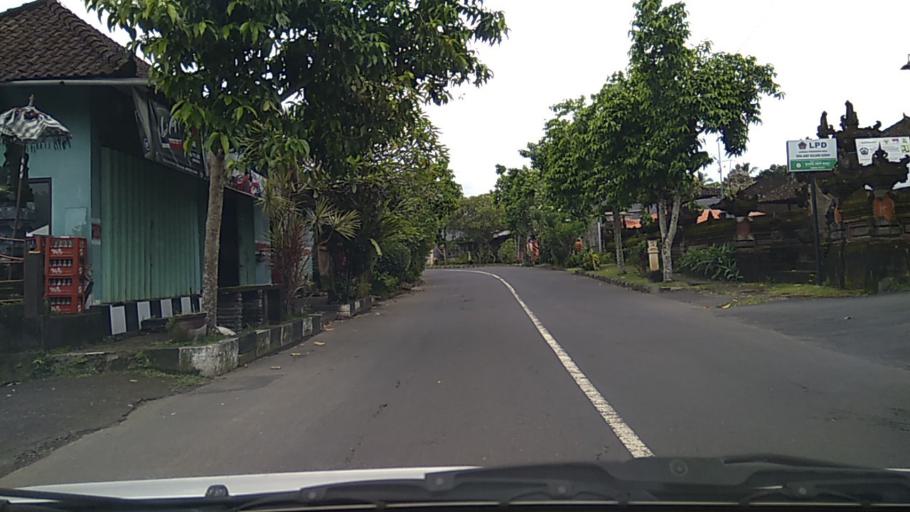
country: ID
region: Bali
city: Banjar Kelodan
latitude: -8.5204
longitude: 115.3457
